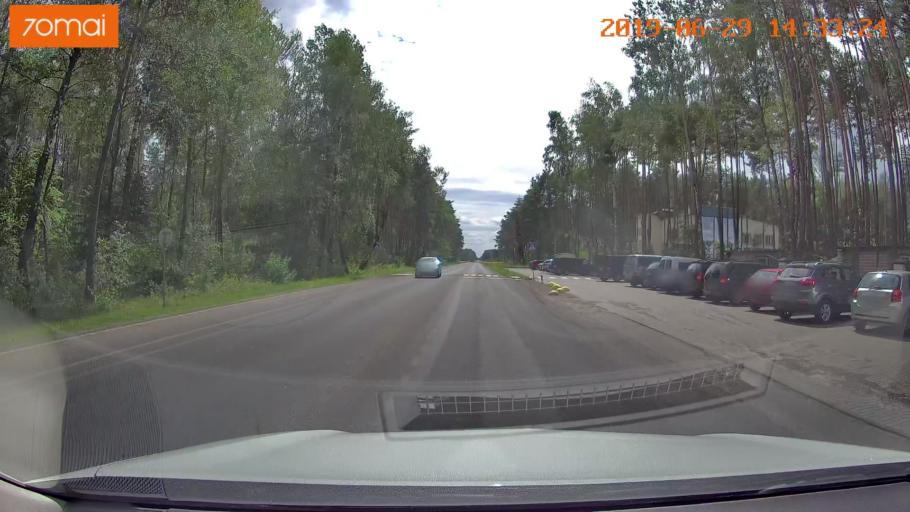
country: BY
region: Minsk
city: Salihorsk
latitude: 52.7782
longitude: 27.5012
